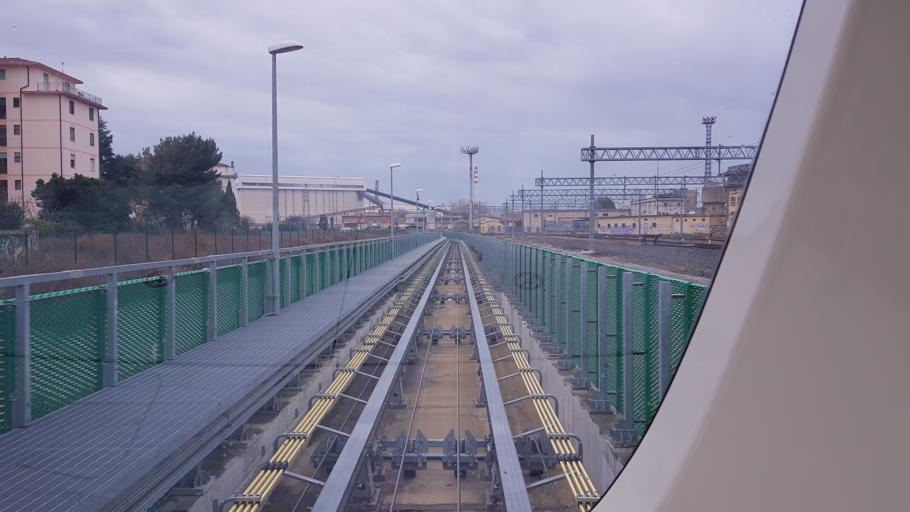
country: IT
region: Tuscany
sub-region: Province of Pisa
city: Pisa
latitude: 43.7077
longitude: 10.3960
